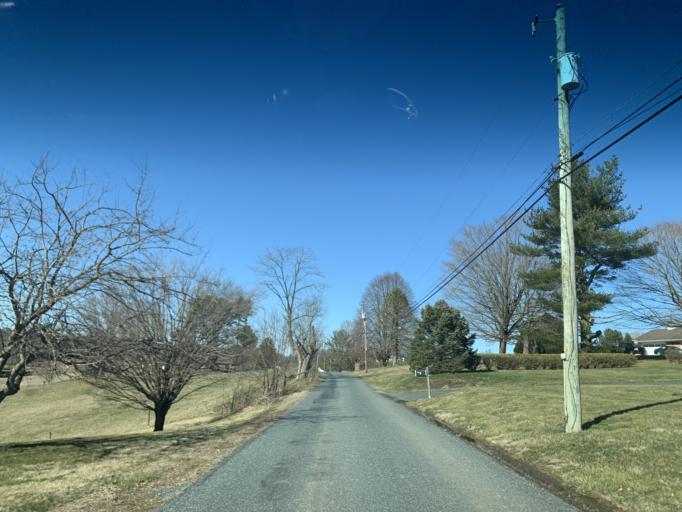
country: US
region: Maryland
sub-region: Harford County
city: Aberdeen
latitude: 39.6284
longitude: -76.2122
